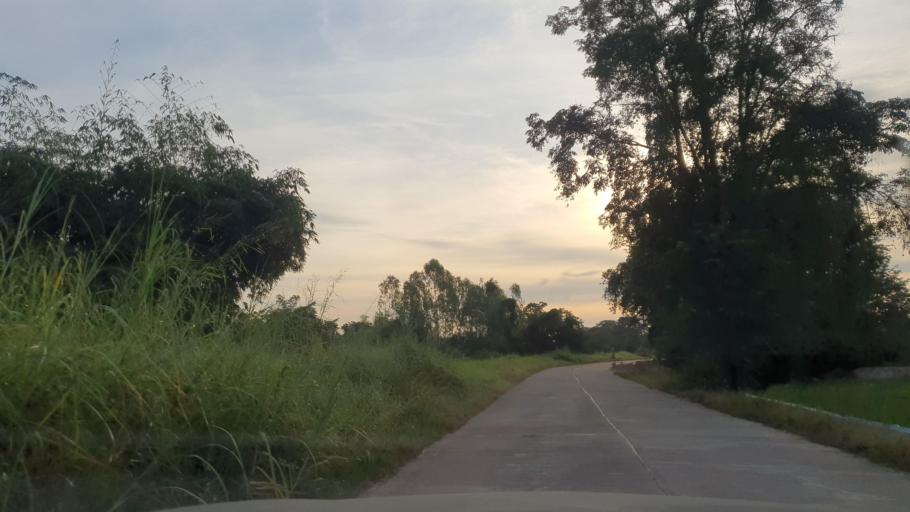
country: TH
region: Nakhon Sawan
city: Krok Phra
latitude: 15.6622
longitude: 100.0165
